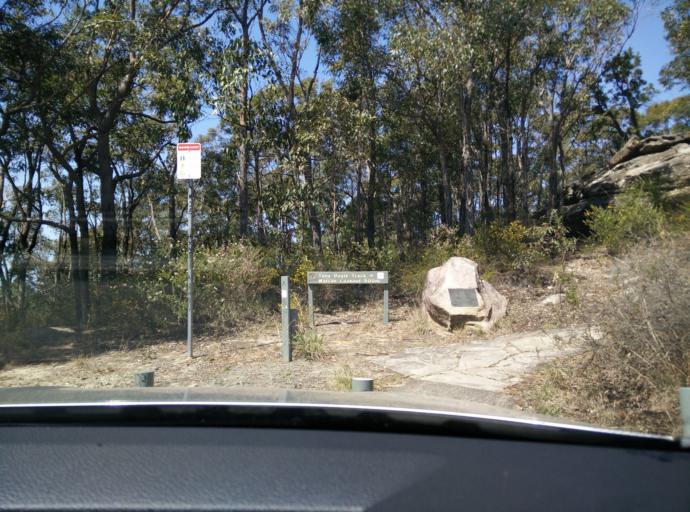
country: AU
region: New South Wales
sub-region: Gosford Shire
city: Umina
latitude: -33.5499
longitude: 151.2880
